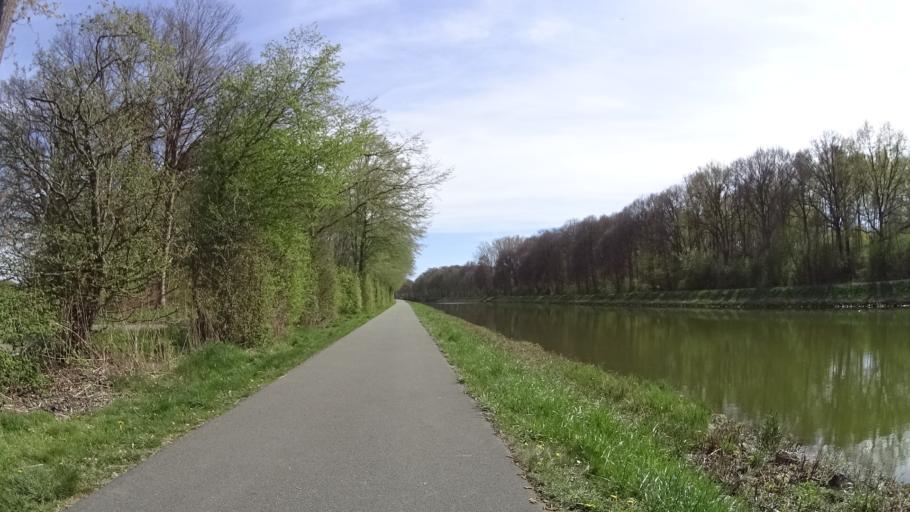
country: DE
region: North Rhine-Westphalia
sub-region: Regierungsbezirk Munster
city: Dreierwalde
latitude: 52.3115
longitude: 7.4677
